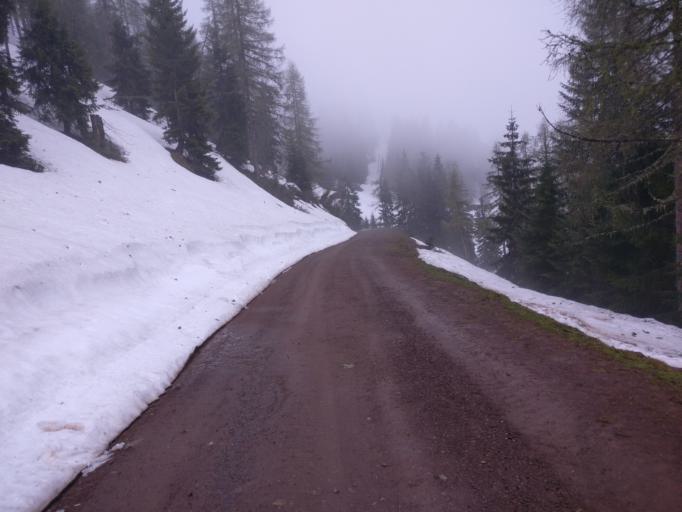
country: AT
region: Salzburg
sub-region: Politischer Bezirk Sankt Johann im Pongau
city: Werfenweng
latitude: 47.4722
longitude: 13.2976
